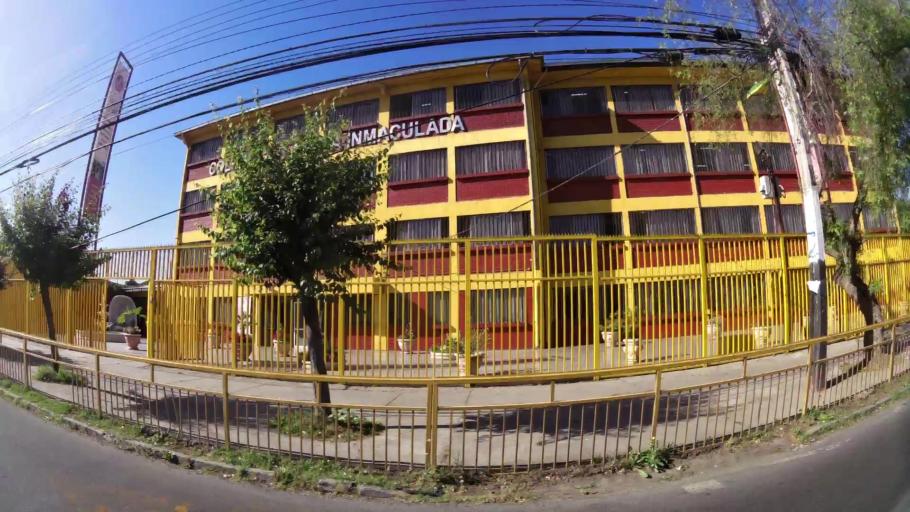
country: CL
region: Santiago Metropolitan
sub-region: Provincia de Maipo
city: San Bernardo
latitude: -33.5522
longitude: -70.6749
